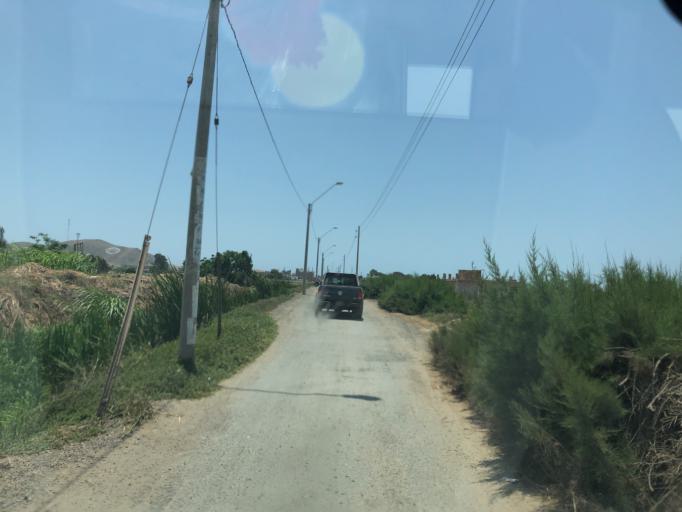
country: PE
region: Lima
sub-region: Provincia de Canete
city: San Vicente de Canete
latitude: -13.0230
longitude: -76.4710
